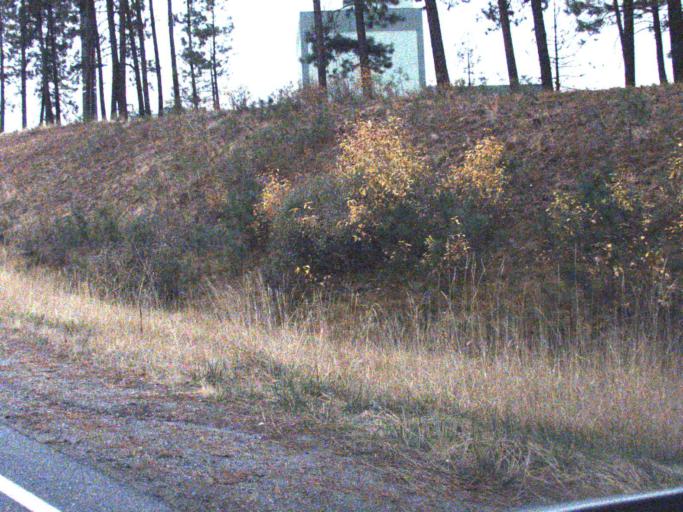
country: US
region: Washington
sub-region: Stevens County
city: Kettle Falls
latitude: 48.6222
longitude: -118.1102
